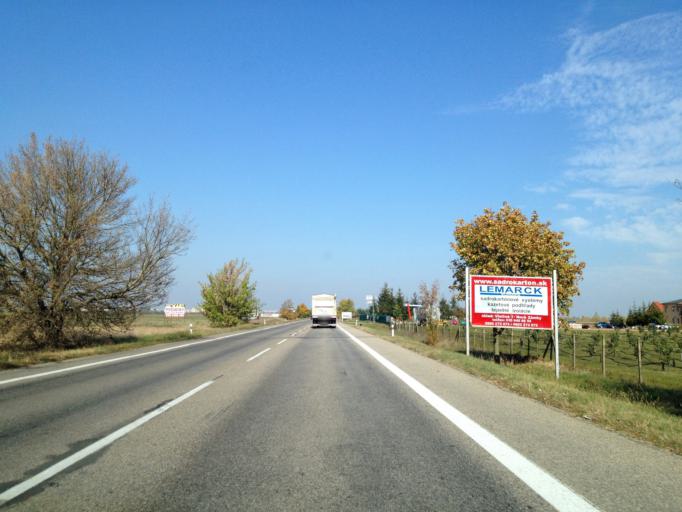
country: SK
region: Nitriansky
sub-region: Okres Nove Zamky
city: Nove Zamky
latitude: 47.9548
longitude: 18.1916
